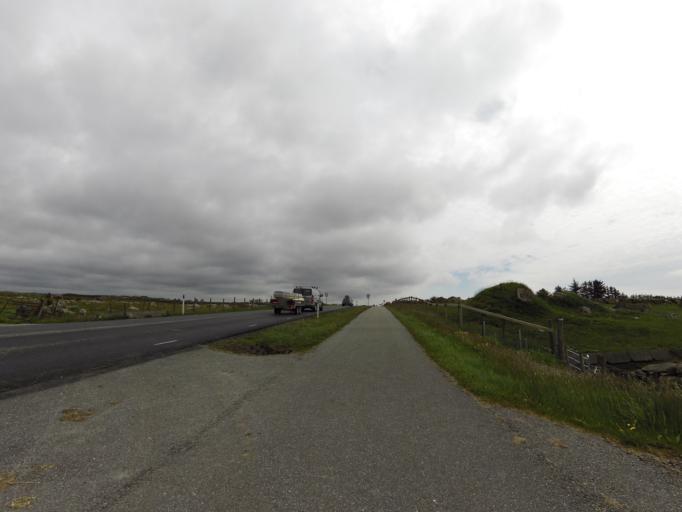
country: NO
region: Rogaland
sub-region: Ha
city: Naerbo
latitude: 58.6435
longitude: 5.6042
